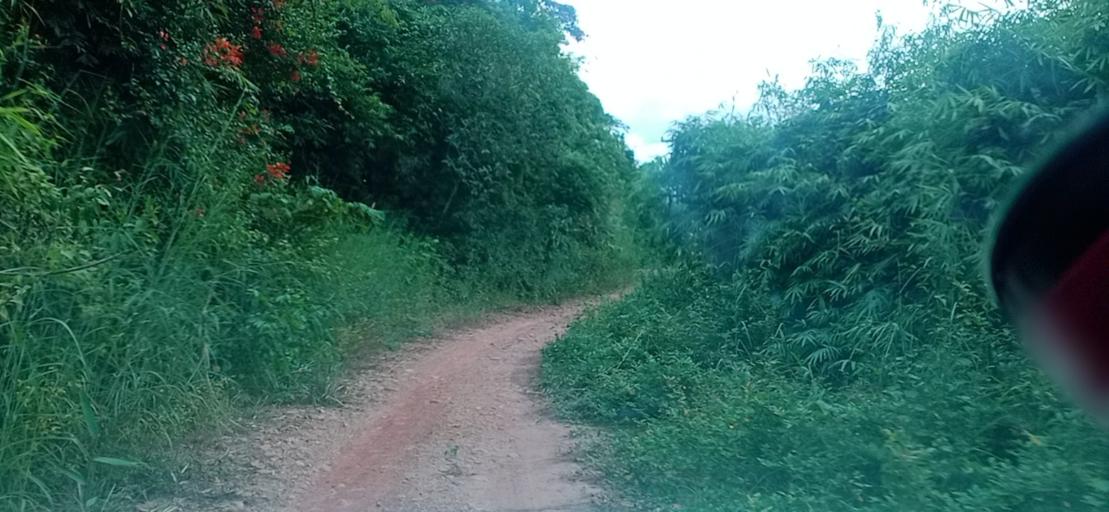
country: TH
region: Changwat Bueng Kan
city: Pak Khat
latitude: 18.5619
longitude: 103.2653
